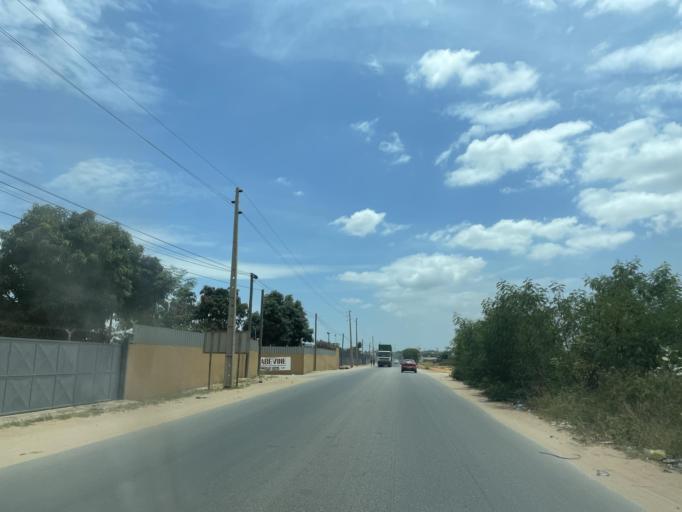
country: AO
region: Luanda
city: Luanda
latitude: -8.9388
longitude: 13.3888
